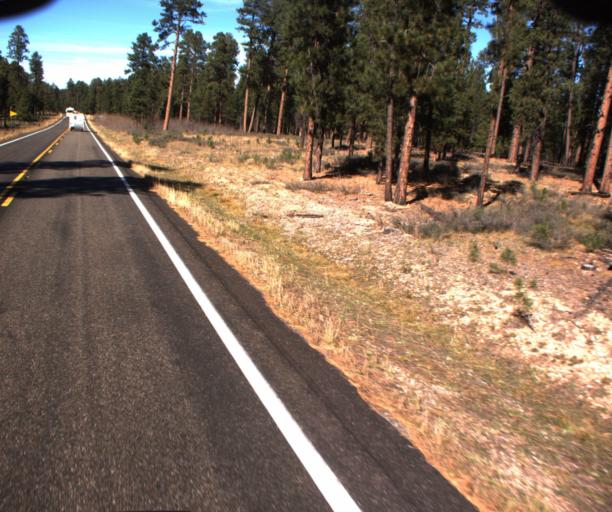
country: US
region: Arizona
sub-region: Coconino County
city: Fredonia
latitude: 36.6739
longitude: -112.2085
